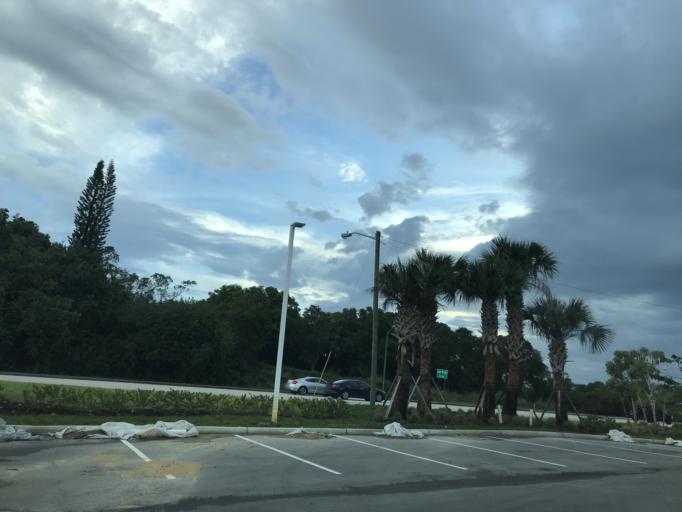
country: US
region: Florida
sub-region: Palm Beach County
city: Hypoluxo
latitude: 26.5728
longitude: -80.0727
